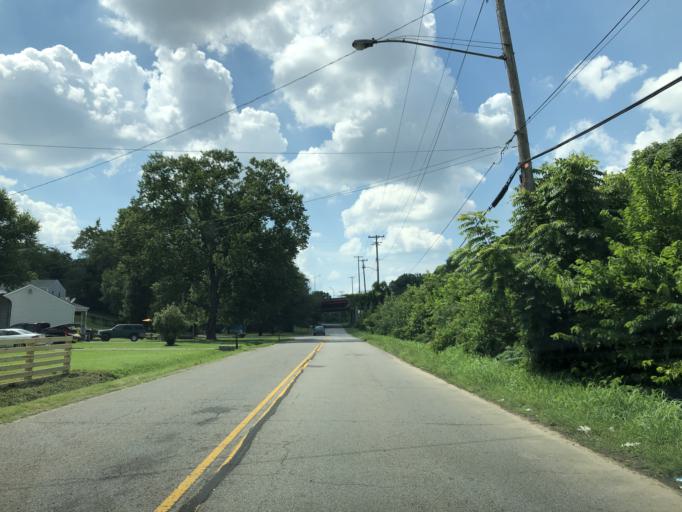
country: US
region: Tennessee
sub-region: Davidson County
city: Oak Hill
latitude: 36.1231
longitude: -86.7361
